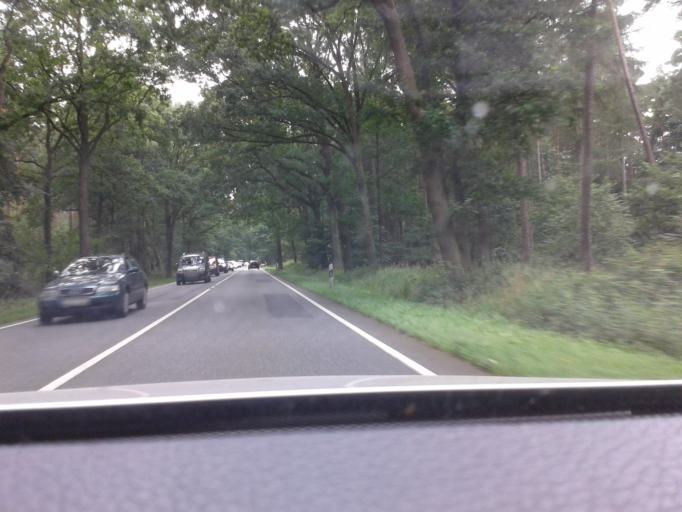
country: DE
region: Lower Saxony
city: Haenigsen
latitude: 52.4506
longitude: 10.0715
